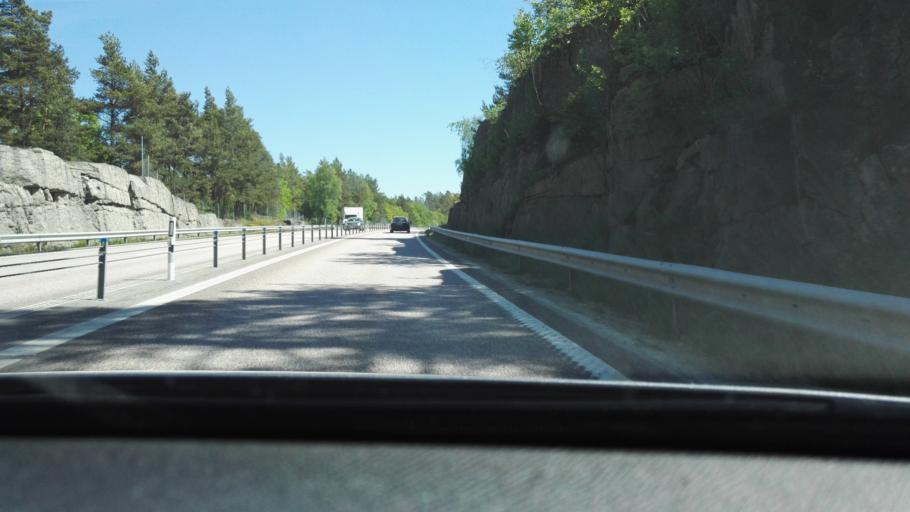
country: SE
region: Blekinge
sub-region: Ronneby Kommun
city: Kallinge
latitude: 56.2131
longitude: 15.3146
